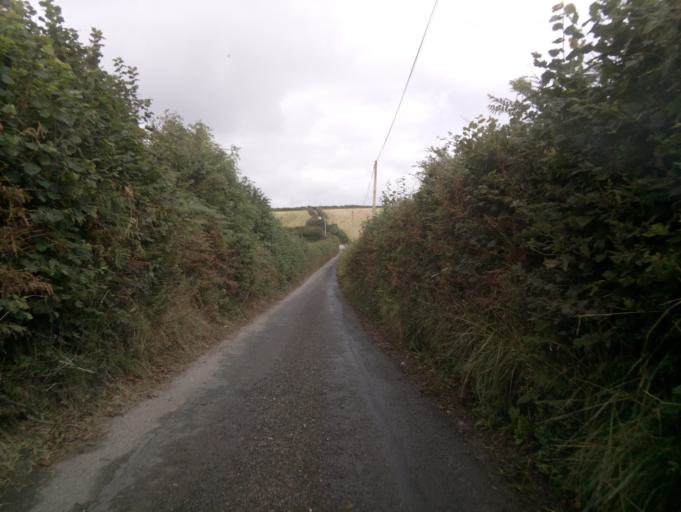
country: GB
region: England
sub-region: Devon
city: Dartmouth
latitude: 50.3339
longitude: -3.5871
